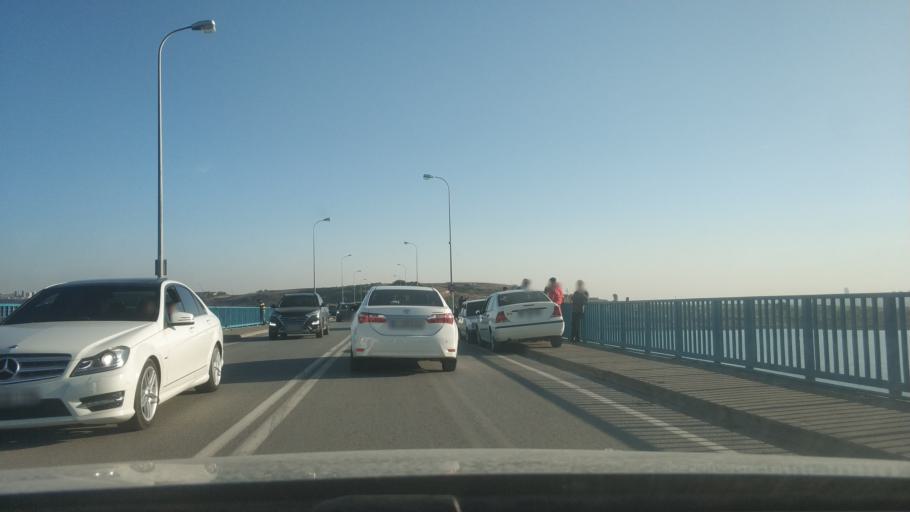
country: TR
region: Adana
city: Adana
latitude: 37.1022
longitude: 35.3011
